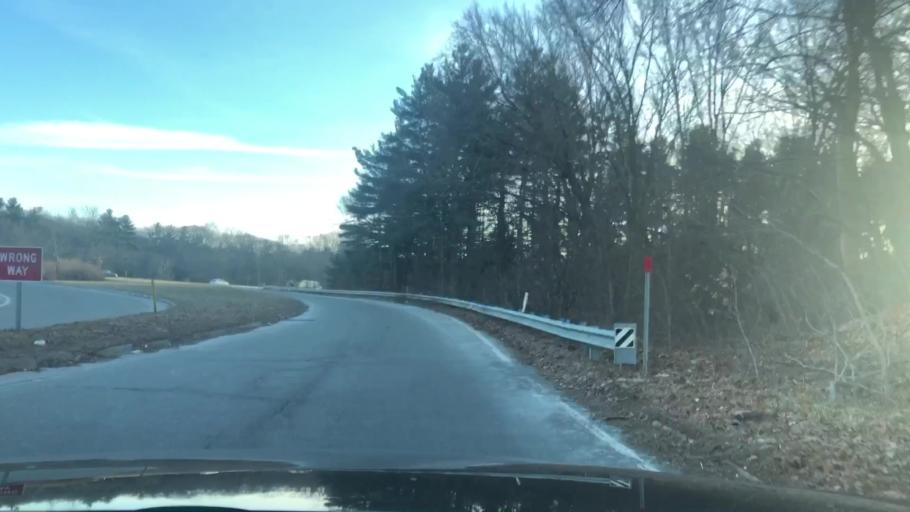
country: US
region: Massachusetts
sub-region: Worcester County
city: Bolton
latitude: 42.4307
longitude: -71.5952
